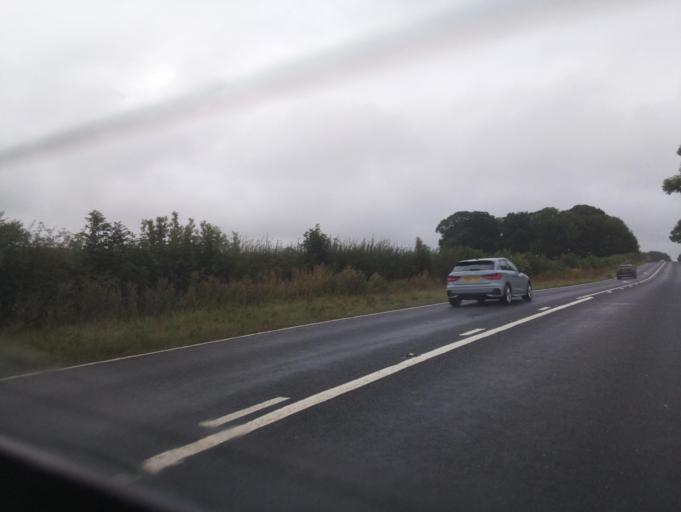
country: GB
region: England
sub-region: North Yorkshire
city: Pannal
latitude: 53.9244
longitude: -1.5324
